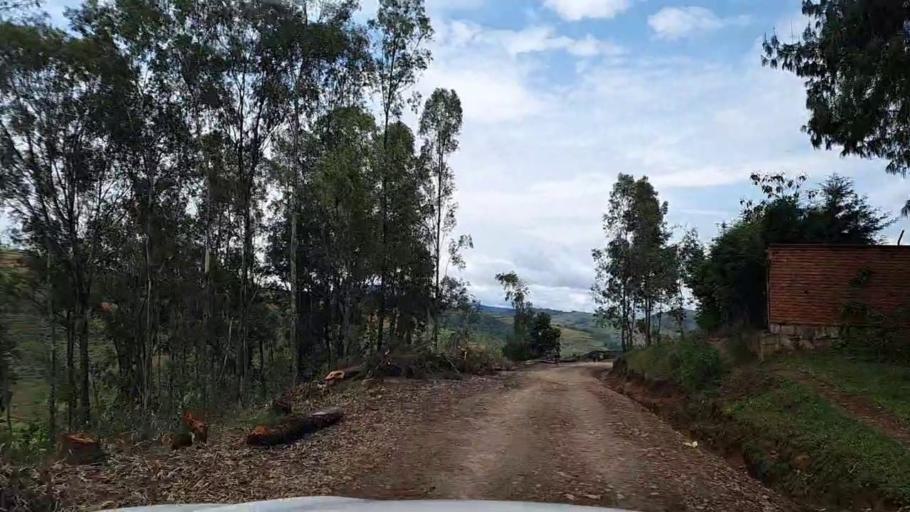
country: RW
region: Southern Province
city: Gikongoro
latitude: -2.3337
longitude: 29.5236
